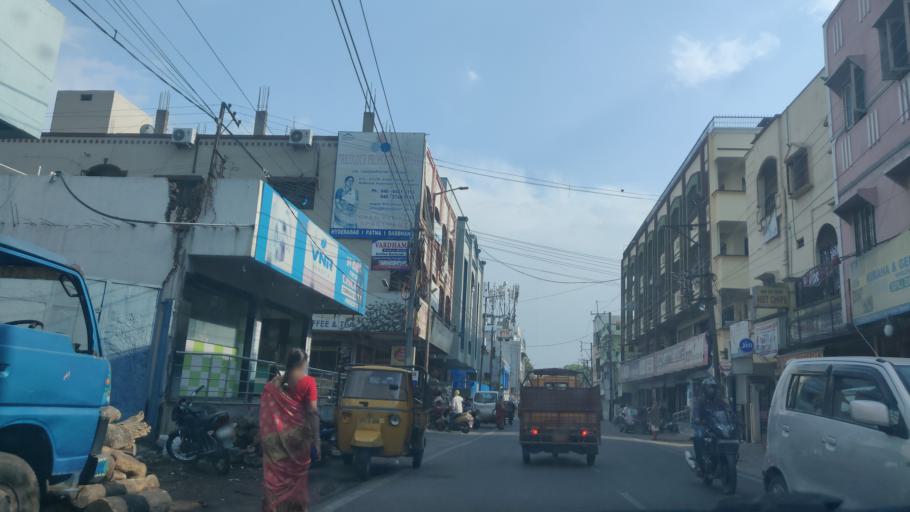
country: IN
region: Telangana
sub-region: Rangareddi
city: Gaddi Annaram
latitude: 17.3891
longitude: 78.5112
